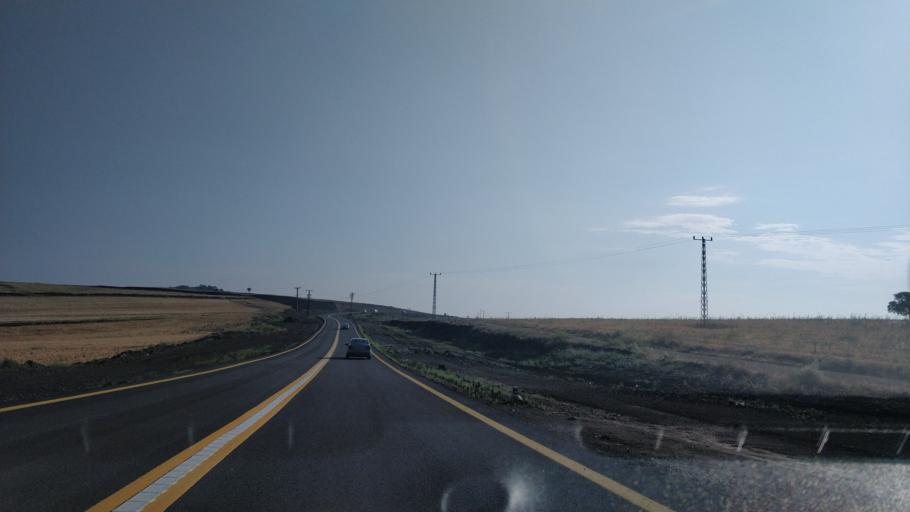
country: TR
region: Ankara
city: Etimesgut
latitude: 39.8588
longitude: 32.5707
